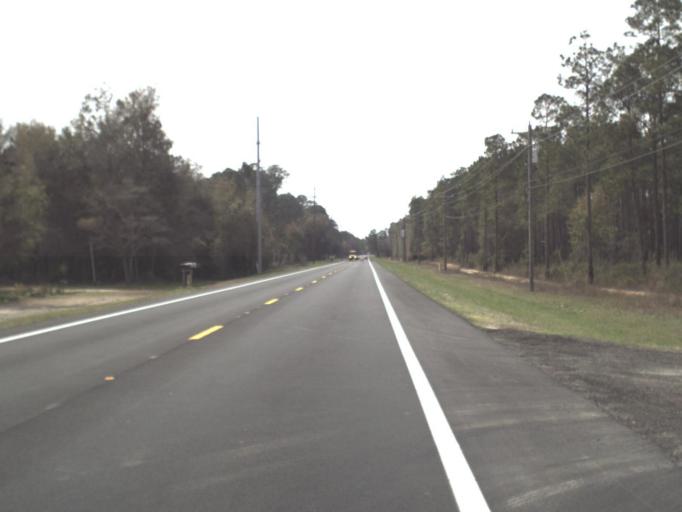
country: US
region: Florida
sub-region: Gadsden County
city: Midway
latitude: 30.4412
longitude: -84.4431
